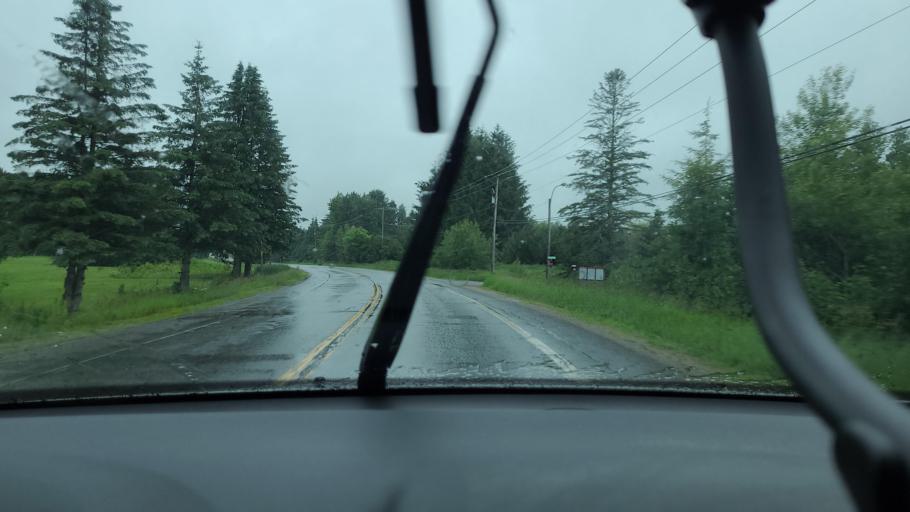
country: CA
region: Quebec
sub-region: Outaouais
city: Saint-Andre-Avellin
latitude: 45.7972
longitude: -75.0671
